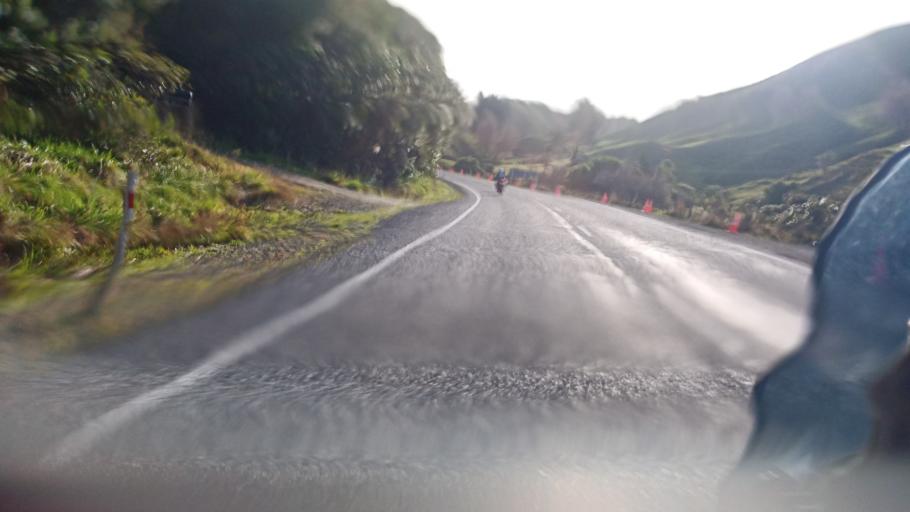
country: NZ
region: Gisborne
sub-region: Gisborne District
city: Gisborne
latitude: -38.4350
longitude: 177.5750
